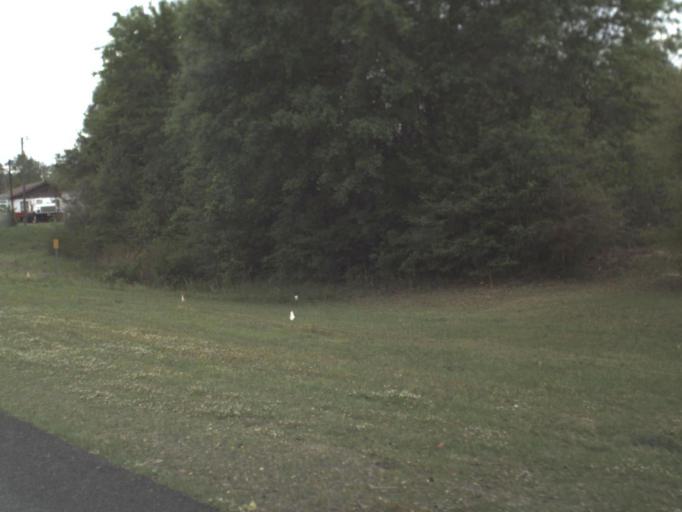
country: US
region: Florida
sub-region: Escambia County
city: Century
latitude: 30.8713
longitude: -87.3223
